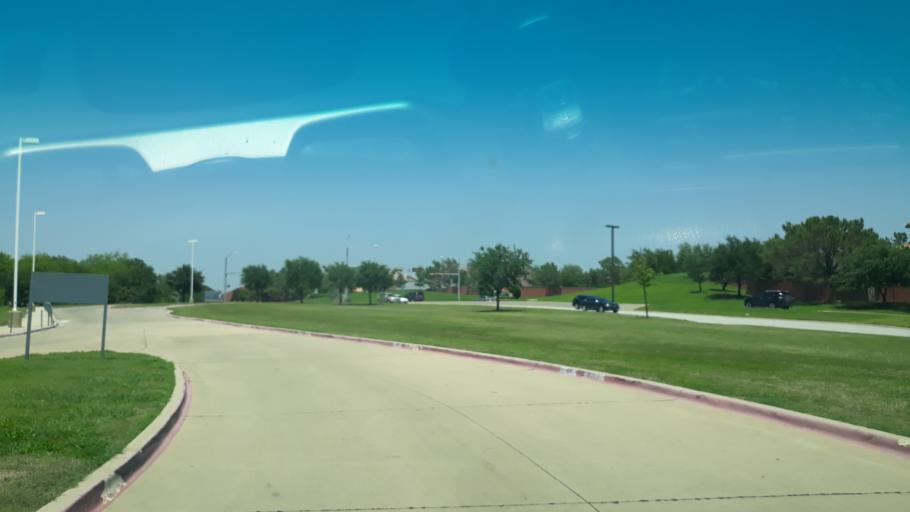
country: US
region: Texas
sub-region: Dallas County
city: Irving
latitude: 32.8692
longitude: -96.9599
